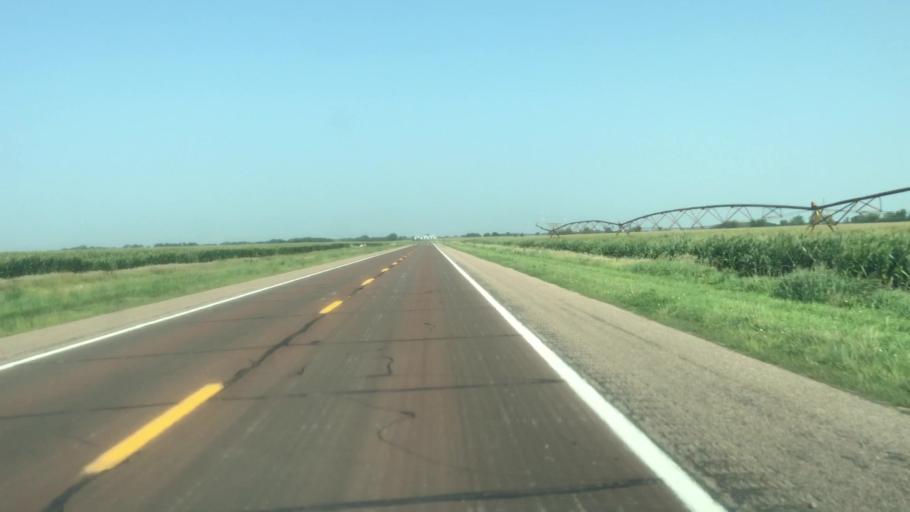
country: US
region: Nebraska
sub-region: Hall County
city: Wood River
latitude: 40.9773
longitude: -98.5159
